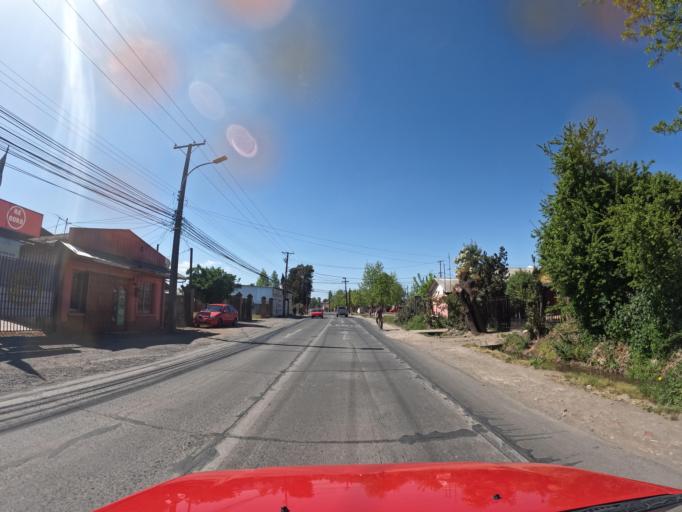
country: CL
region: Maule
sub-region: Provincia de Curico
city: Molina
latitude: -35.0741
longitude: -71.2571
